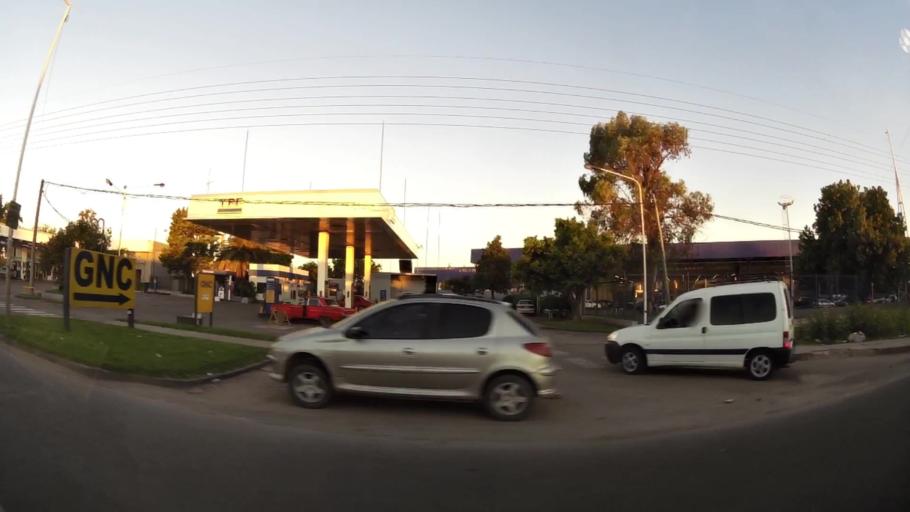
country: AR
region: Buenos Aires
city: Pontevedra
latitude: -34.7539
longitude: -58.6142
